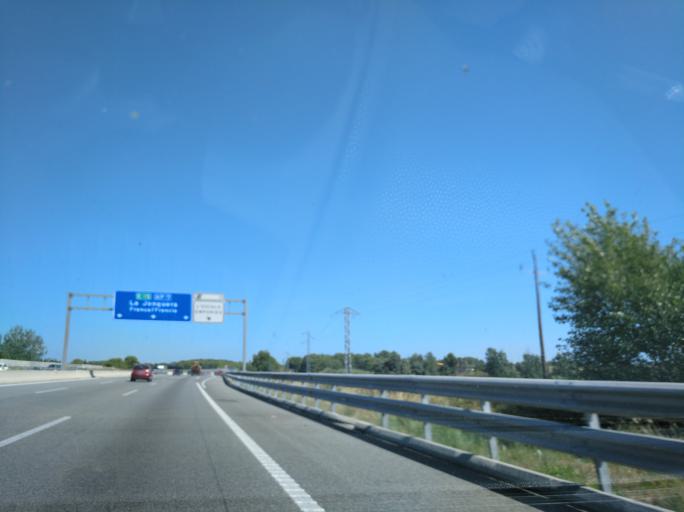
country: ES
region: Catalonia
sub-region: Provincia de Girona
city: Vilademuls
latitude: 42.1255
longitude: 2.9119
